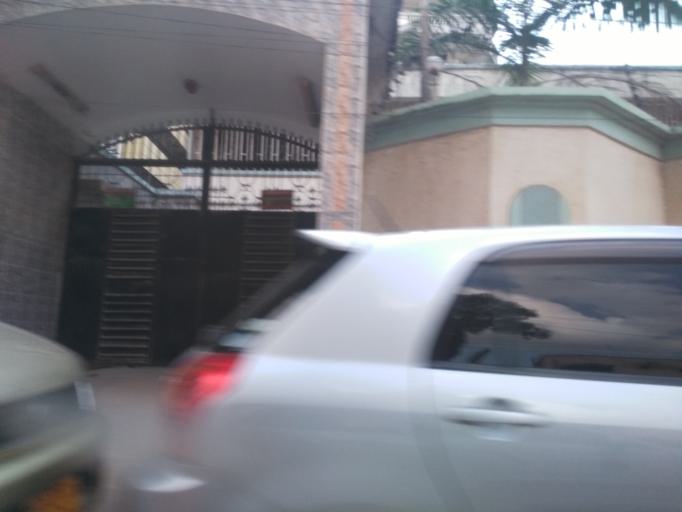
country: TZ
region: Dar es Salaam
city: Dar es Salaam
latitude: -6.8011
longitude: 39.2759
